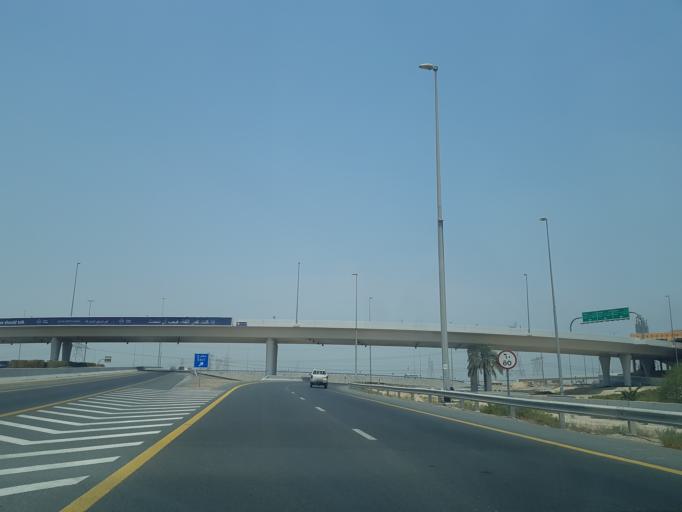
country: AE
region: Ash Shariqah
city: Sharjah
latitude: 25.2123
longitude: 55.4072
